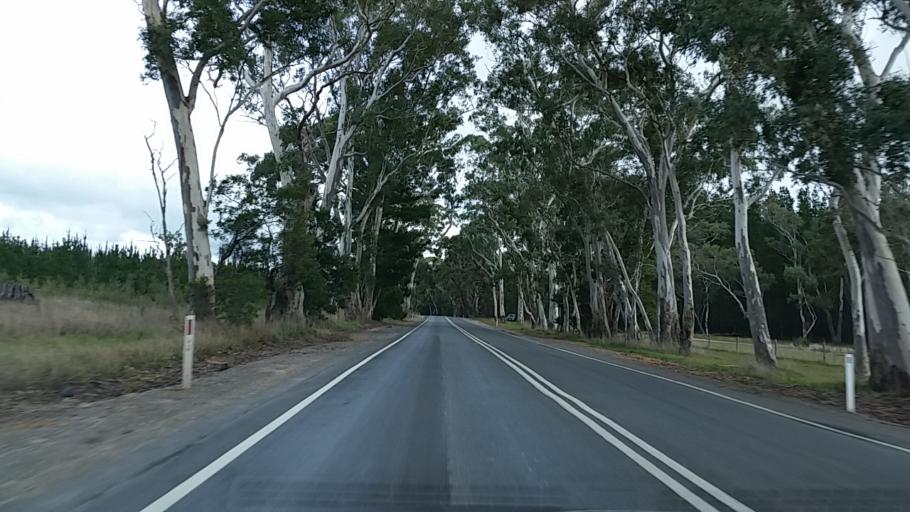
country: AU
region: South Australia
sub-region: Mount Barker
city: Meadows
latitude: -35.2048
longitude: 138.7110
